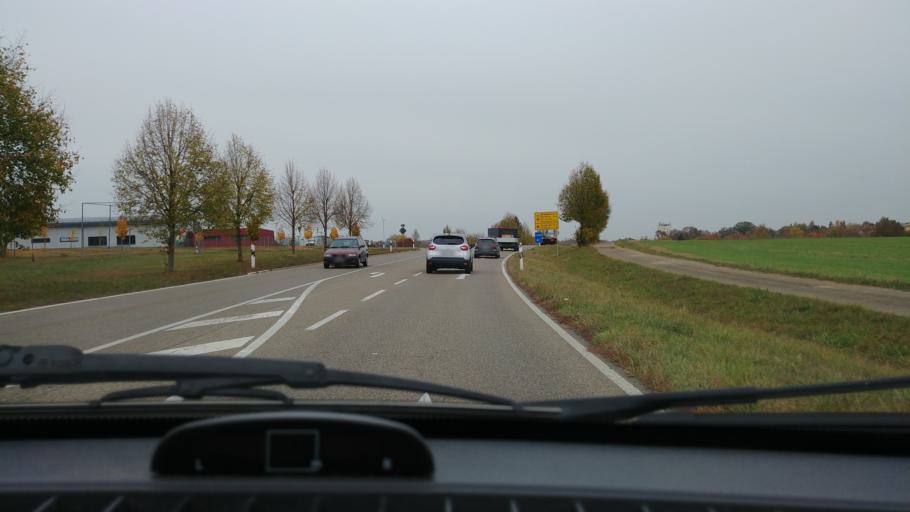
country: DE
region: Baden-Wuerttemberg
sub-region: Regierungsbezirk Stuttgart
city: Rot am See
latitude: 49.2423
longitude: 10.0311
